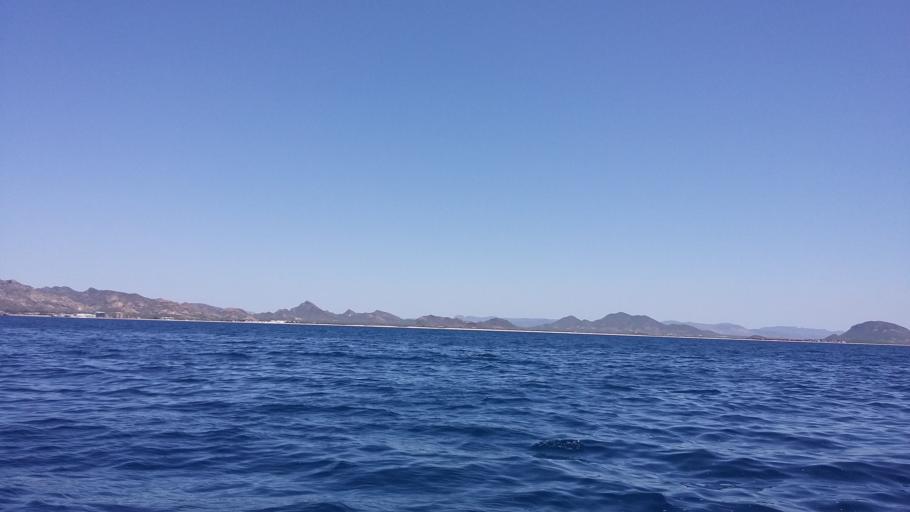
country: MX
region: Sonora
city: Heroica Guaymas
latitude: 27.9292
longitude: -111.0244
